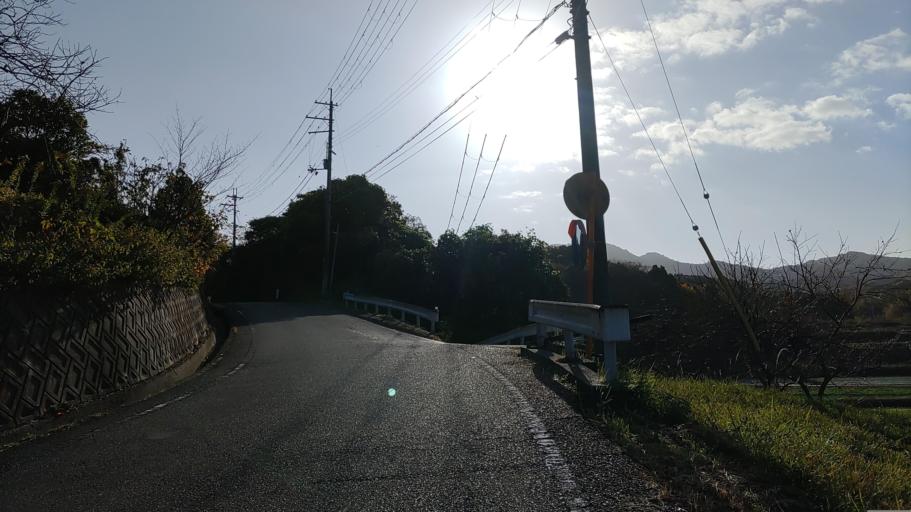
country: JP
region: Hyogo
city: Sumoto
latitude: 34.3902
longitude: 134.8135
